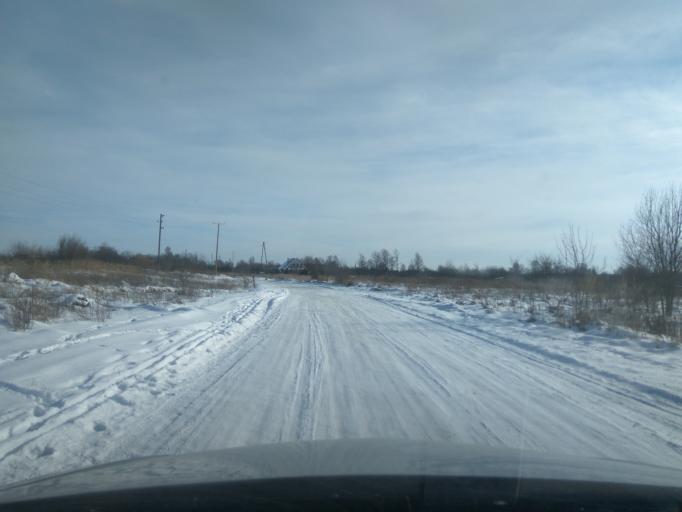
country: LV
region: Kuldigas Rajons
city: Kuldiga
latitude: 56.9834
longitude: 21.9543
